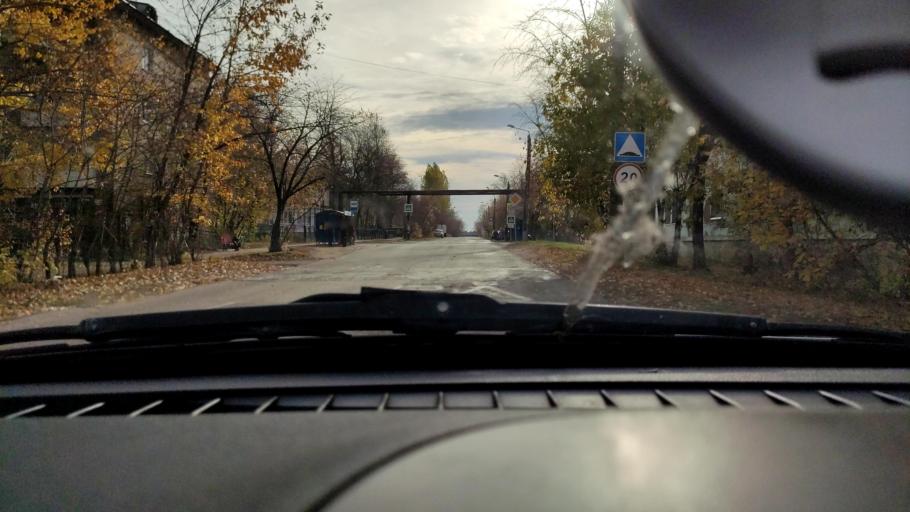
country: RU
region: Perm
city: Perm
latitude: 58.0868
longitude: 56.3910
